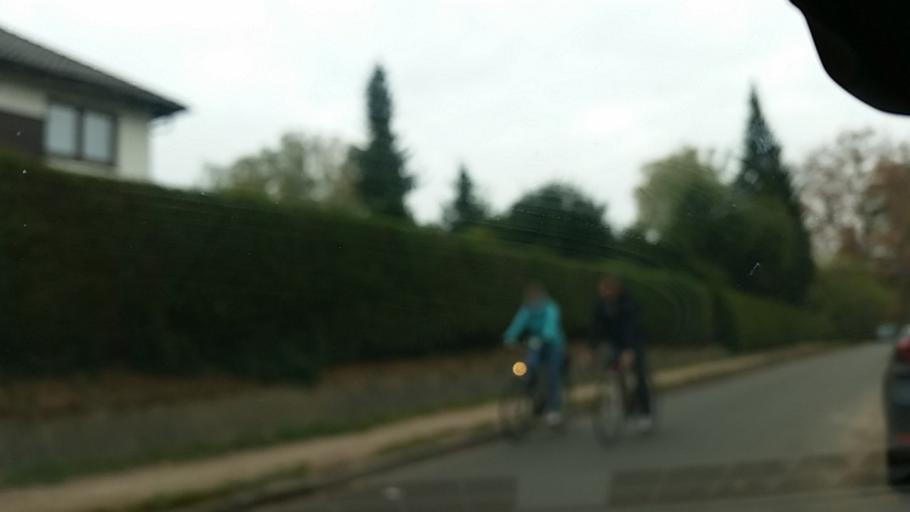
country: DE
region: Schleswig-Holstein
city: Halstenbek
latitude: 53.5599
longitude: 9.8467
